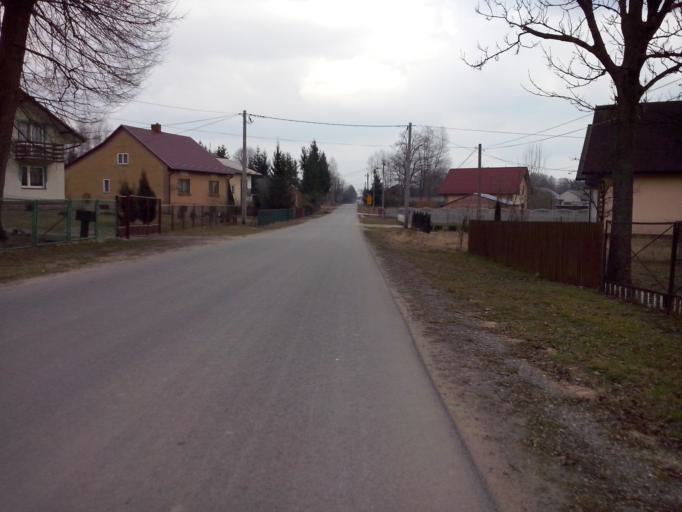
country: PL
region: Subcarpathian Voivodeship
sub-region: Powiat nizanski
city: Krzeszow
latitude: 50.4262
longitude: 22.3480
